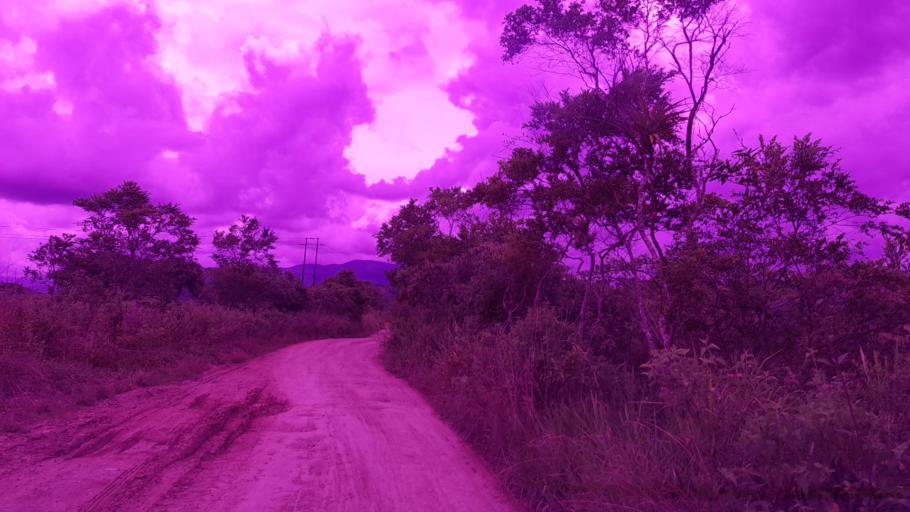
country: CO
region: Valle del Cauca
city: Bugalagrande
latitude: 4.1896
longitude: -76.1401
